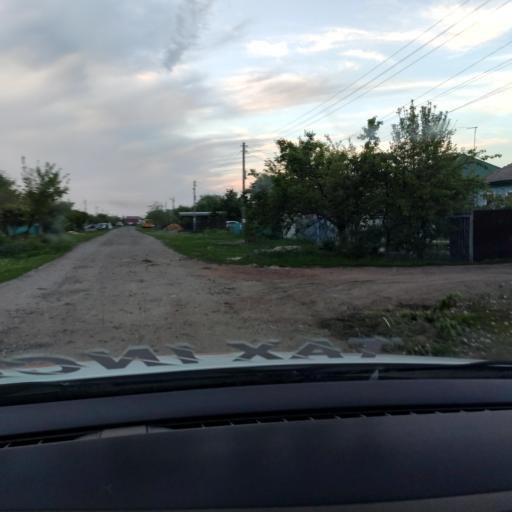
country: RU
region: Voronezj
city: Maslovka
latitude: 51.4532
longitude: 39.2375
